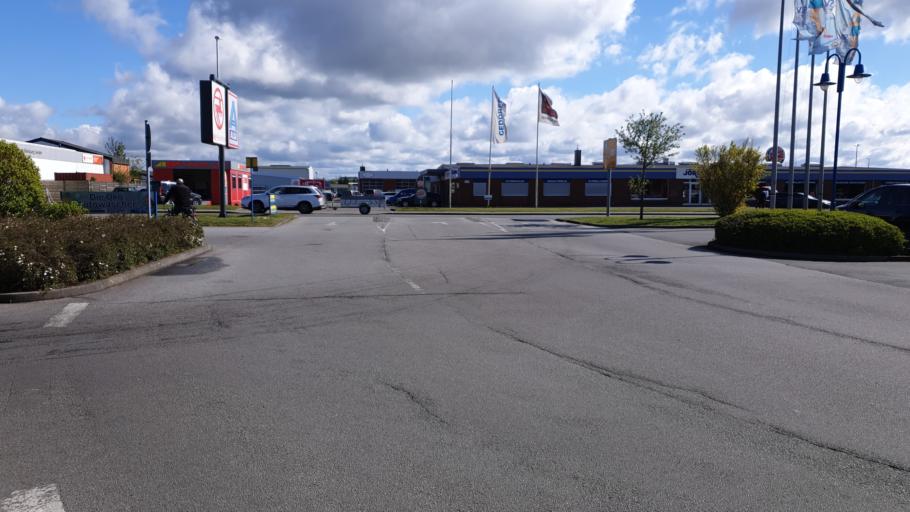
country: DE
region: Schleswig-Holstein
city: Husum
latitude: 54.4899
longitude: 9.0795
